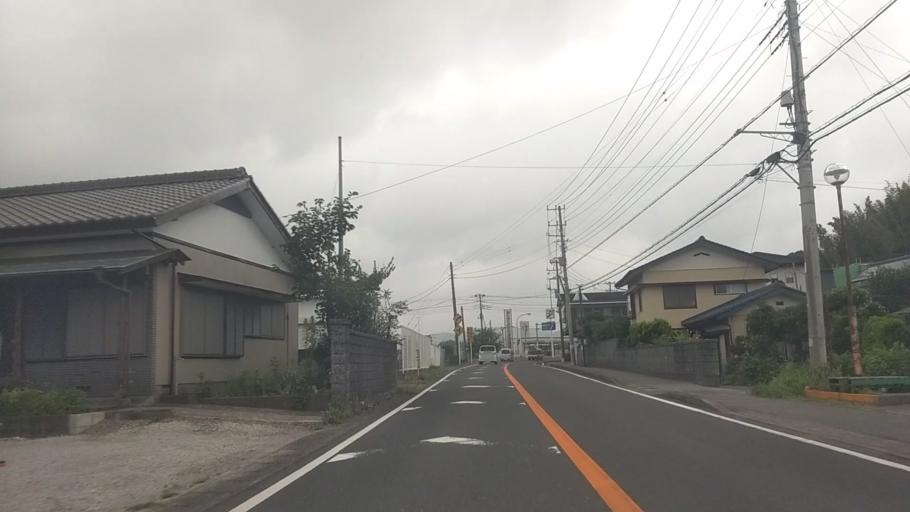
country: JP
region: Chiba
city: Kawaguchi
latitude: 35.1104
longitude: 140.0824
